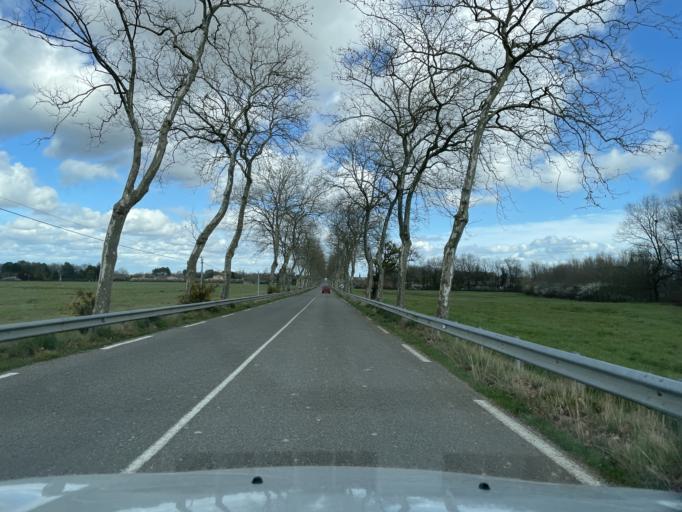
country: FR
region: Midi-Pyrenees
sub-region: Departement de la Haute-Garonne
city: Leguevin
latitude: 43.5939
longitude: 1.1939
